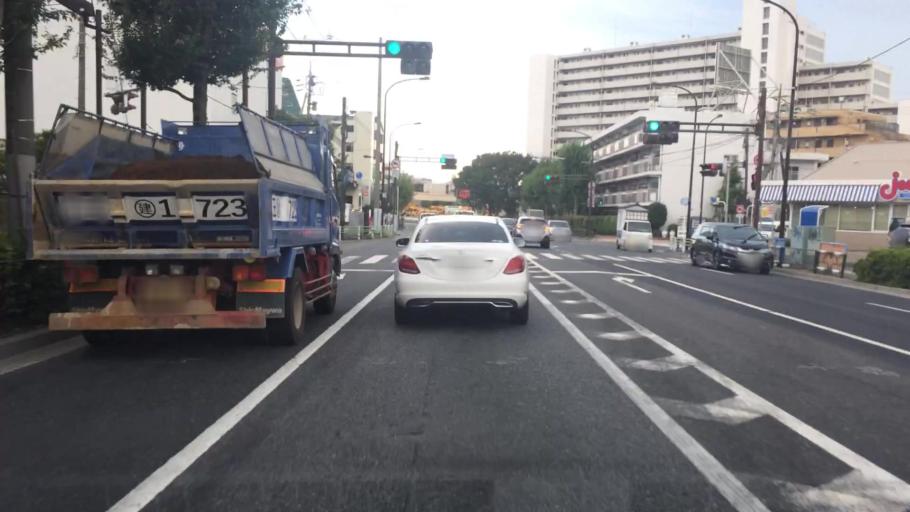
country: JP
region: Tokyo
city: Tokyo
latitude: 35.7286
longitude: 139.6555
